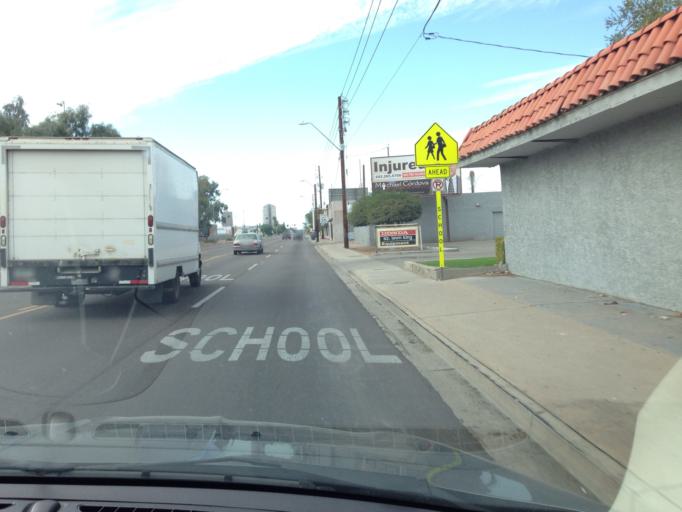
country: US
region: Arizona
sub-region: Maricopa County
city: Phoenix
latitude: 33.4948
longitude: -112.0524
